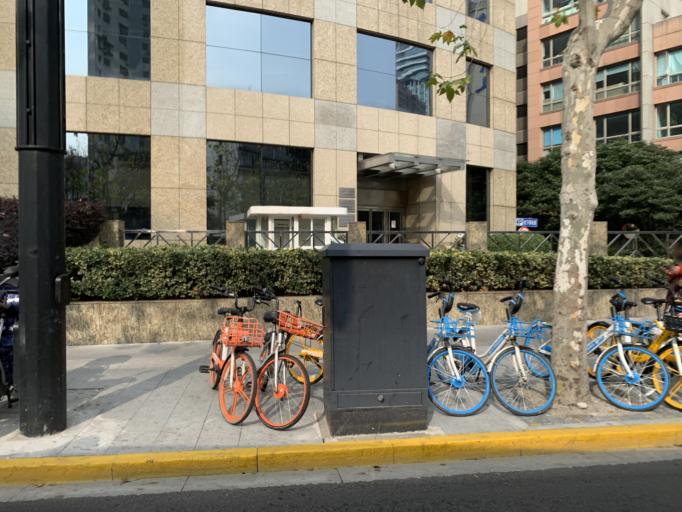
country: CN
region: Shanghai Shi
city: Xuhui
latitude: 31.1999
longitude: 121.4410
